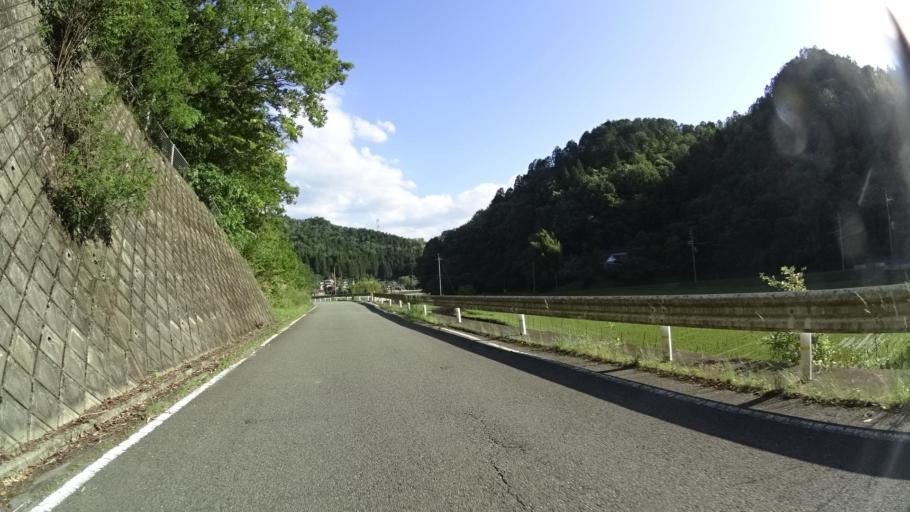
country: JP
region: Kyoto
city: Kameoka
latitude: 34.9689
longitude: 135.5624
